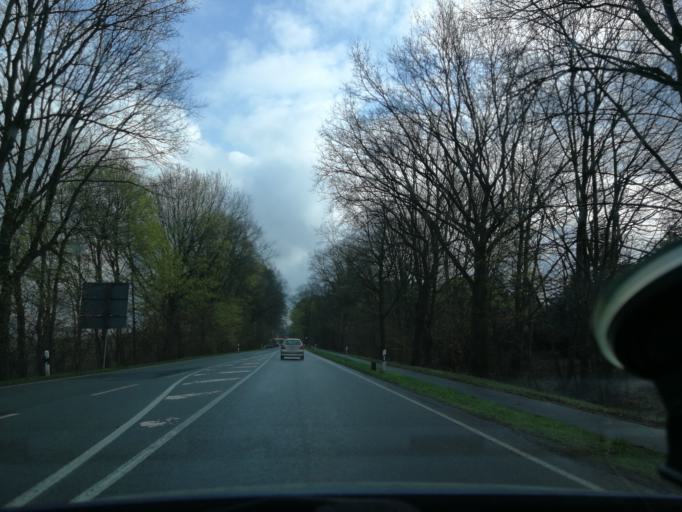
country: DE
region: Lower Saxony
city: Buchholz in der Nordheide
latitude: 53.3313
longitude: 9.8332
